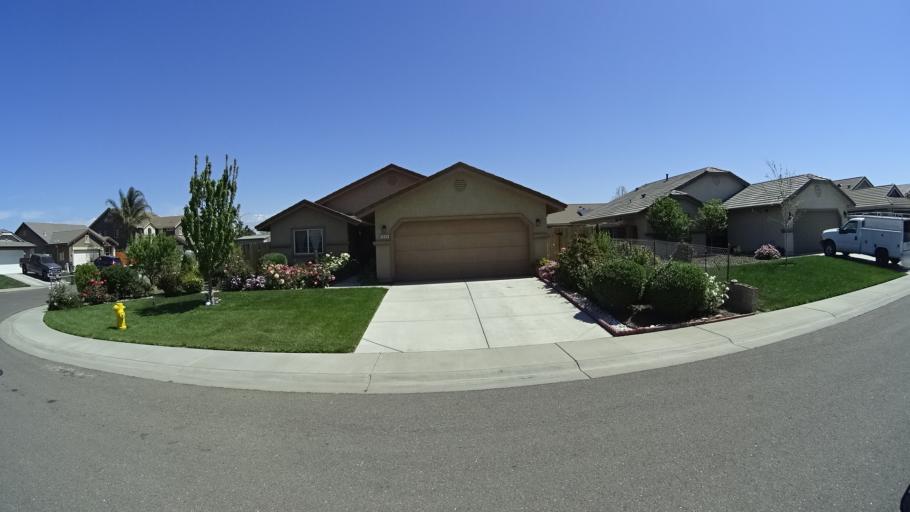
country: US
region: California
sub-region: Glenn County
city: Orland
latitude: 39.7458
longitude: -122.1720
